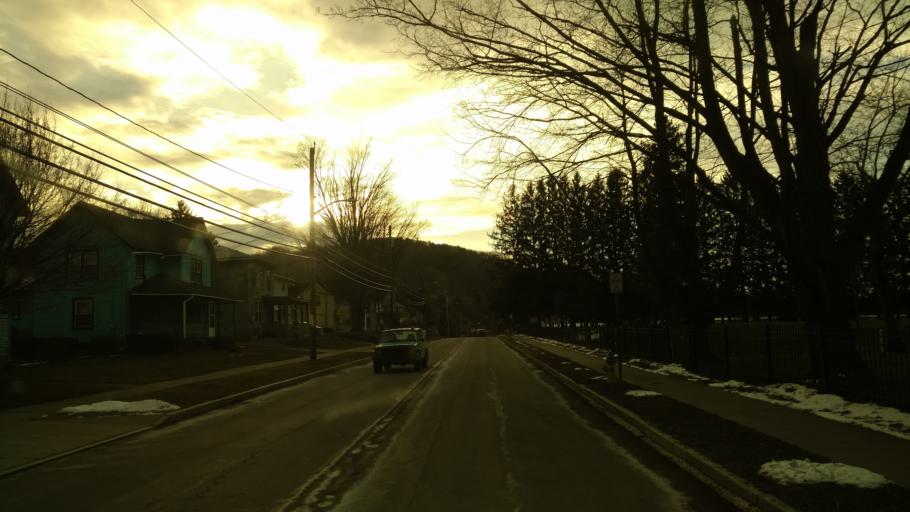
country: US
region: New York
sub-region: Allegany County
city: Wellsville
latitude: 42.1147
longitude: -77.9378
